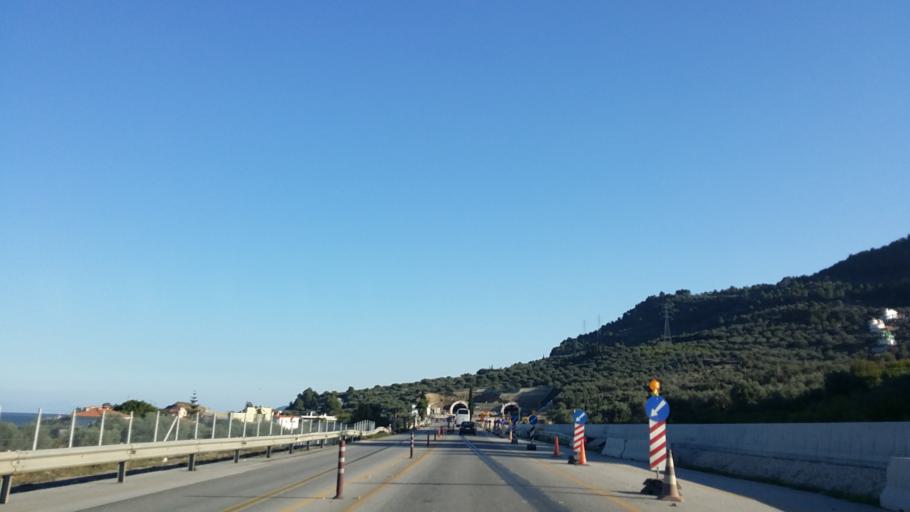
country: GR
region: West Greece
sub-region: Nomos Achaias
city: Aiyira
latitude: 38.1426
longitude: 22.3702
